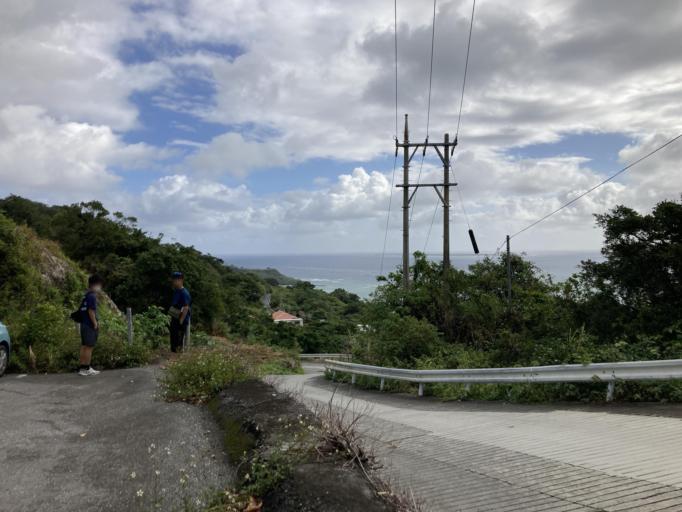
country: JP
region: Okinawa
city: Ginowan
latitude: 26.1617
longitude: 127.8131
